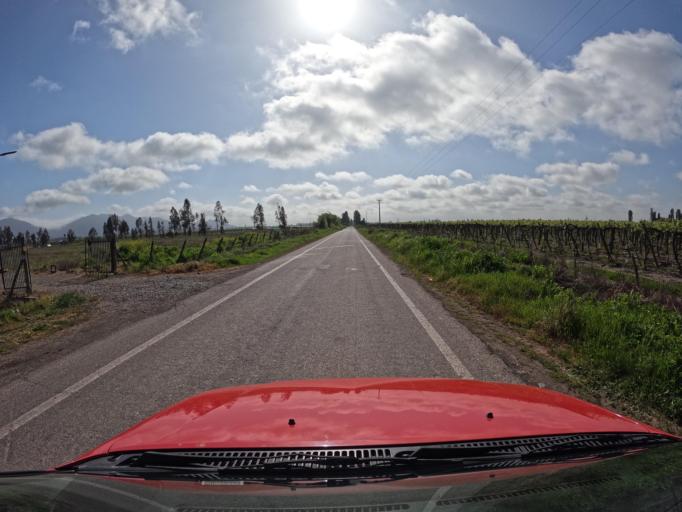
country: CL
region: Maule
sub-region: Provincia de Curico
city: Rauco
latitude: -34.8857
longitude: -71.2564
